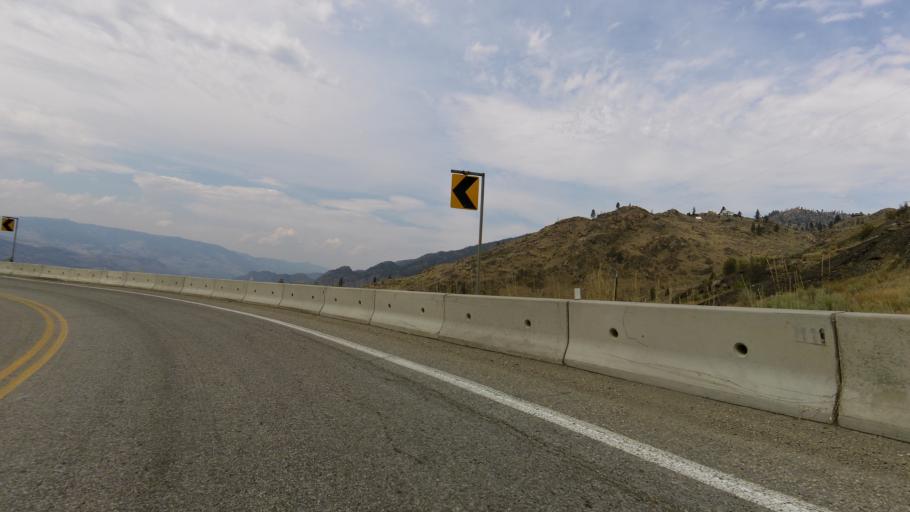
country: CA
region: British Columbia
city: Osoyoos
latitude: 49.0179
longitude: -119.4031
